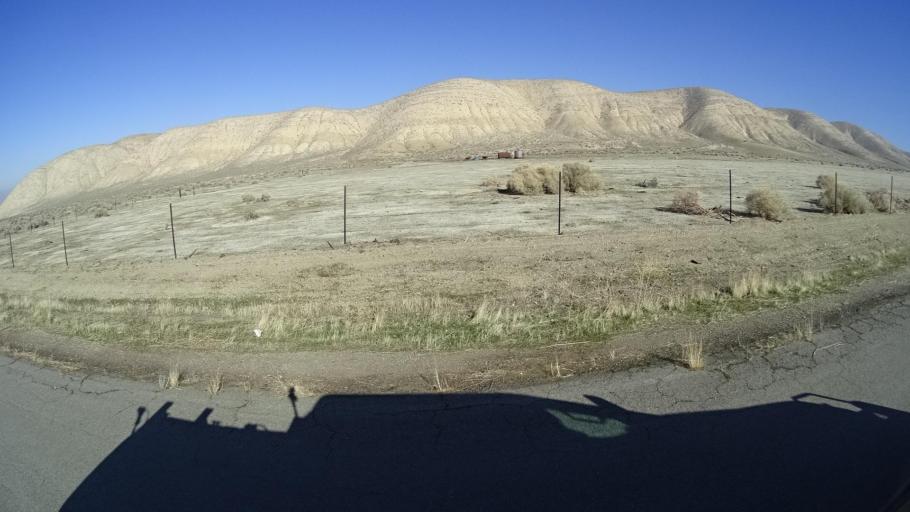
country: US
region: California
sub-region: Kern County
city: Maricopa
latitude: 35.0030
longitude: -119.4061
